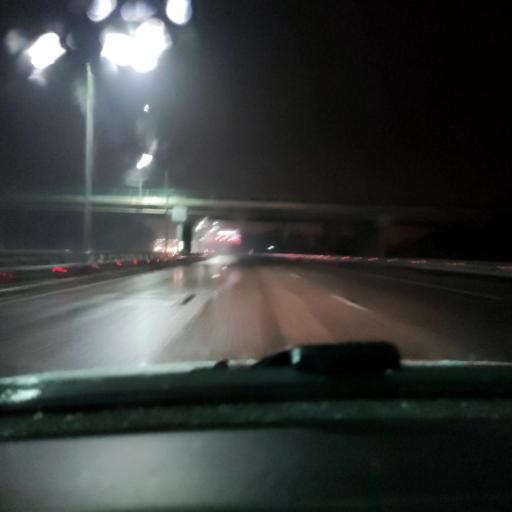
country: RU
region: Voronezj
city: Somovo
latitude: 51.7262
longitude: 39.3112
